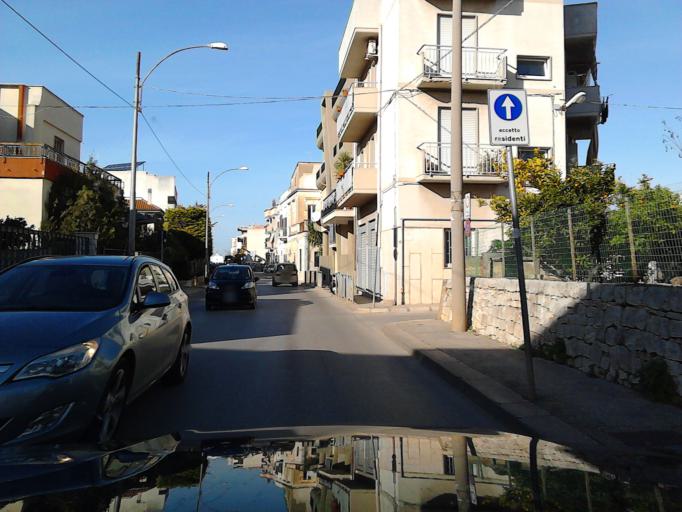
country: IT
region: Apulia
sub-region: Provincia di Bari
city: Rutigliano
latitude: 41.0146
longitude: 17.0014
